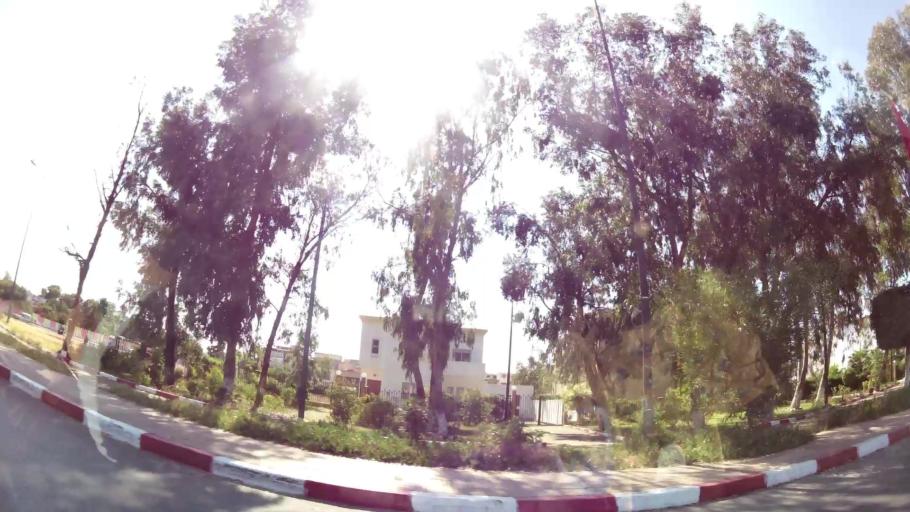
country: MA
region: Rabat-Sale-Zemmour-Zaer
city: Sale
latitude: 34.0425
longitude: -6.7748
